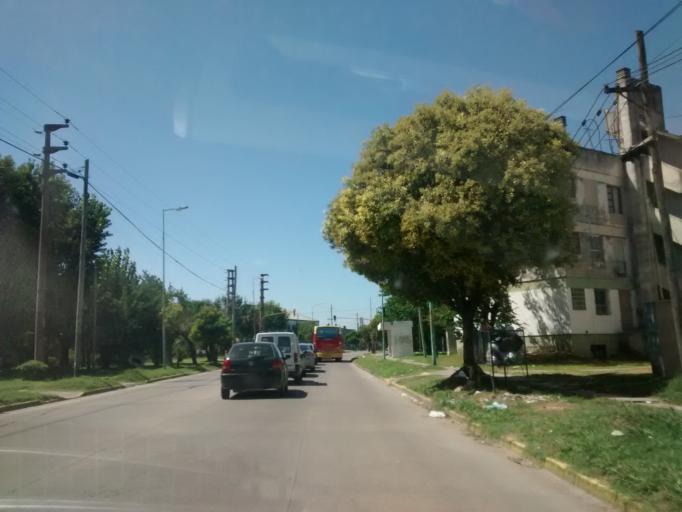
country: AR
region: Buenos Aires
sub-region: Partido de Berisso
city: Berisso
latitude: -34.8776
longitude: -57.8537
